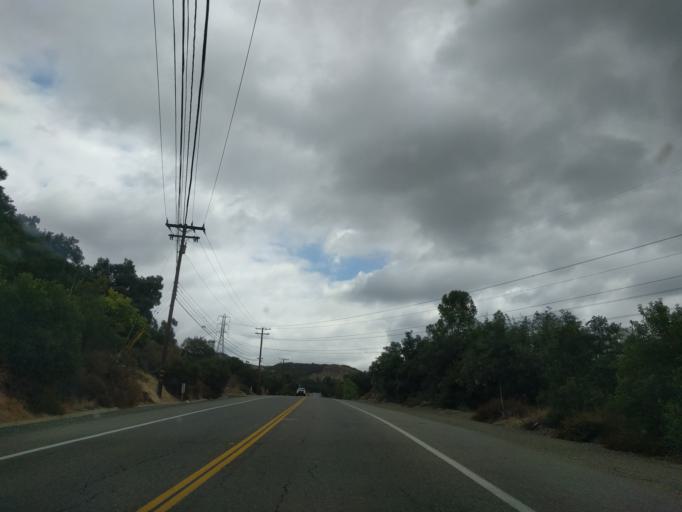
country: US
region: California
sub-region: Orange County
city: Foothill Ranch
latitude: 33.7102
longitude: -117.6447
